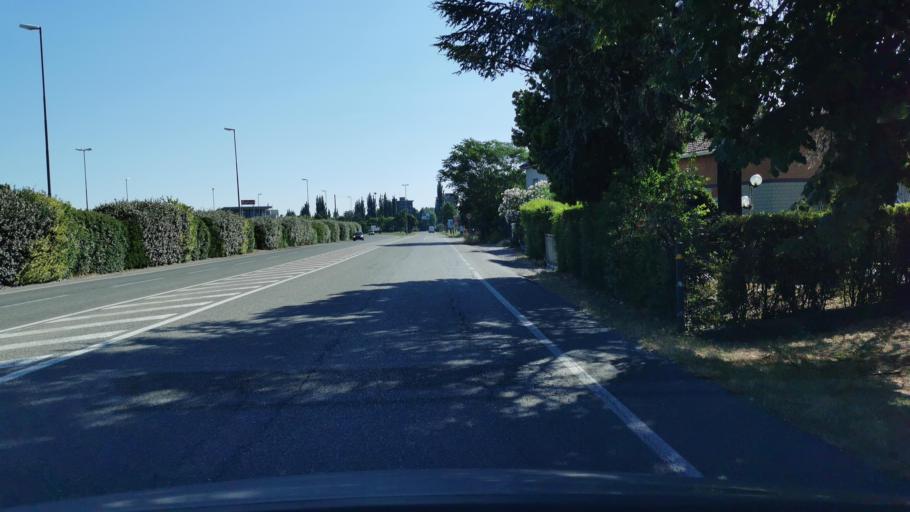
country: IT
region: Emilia-Romagna
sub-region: Provincia di Modena
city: Santa Croce Scuole
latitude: 44.7735
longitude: 10.8584
